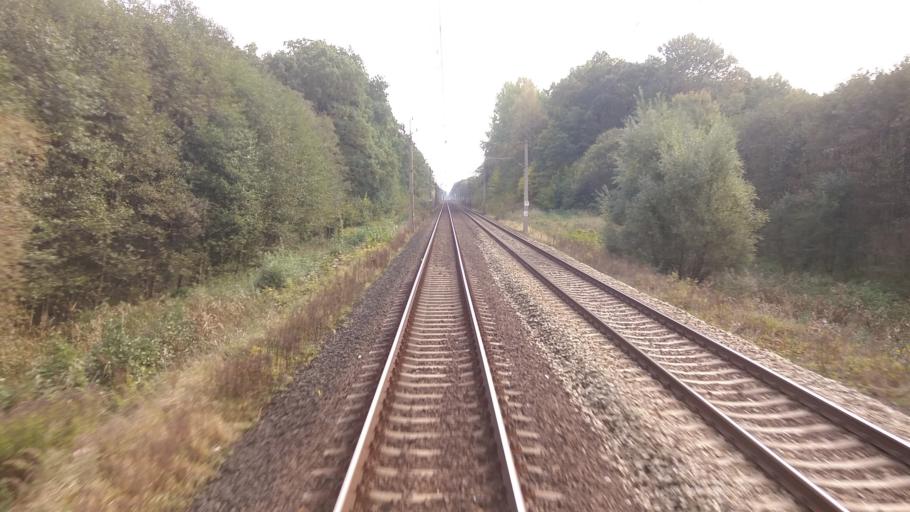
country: PL
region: West Pomeranian Voivodeship
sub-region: Powiat stargardzki
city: Dolice
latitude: 53.1892
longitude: 15.2461
